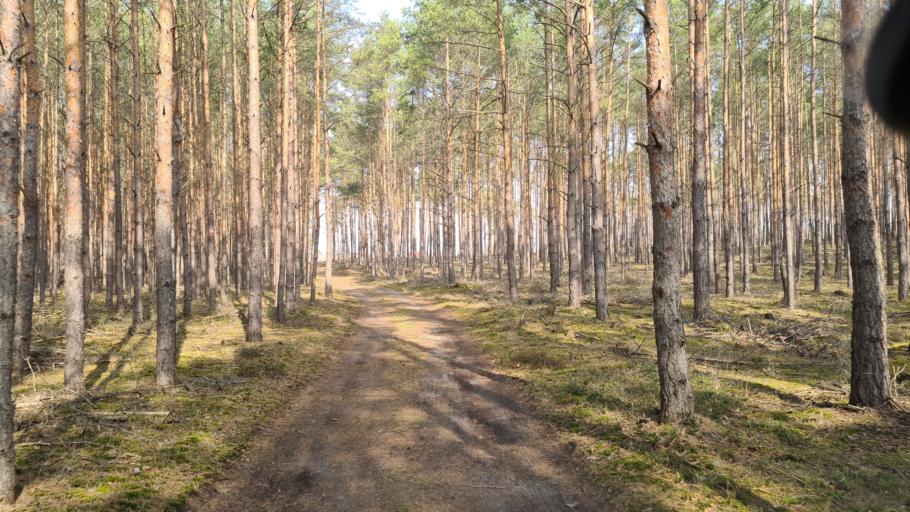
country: DE
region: Brandenburg
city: Schonborn
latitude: 51.6622
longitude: 13.4659
